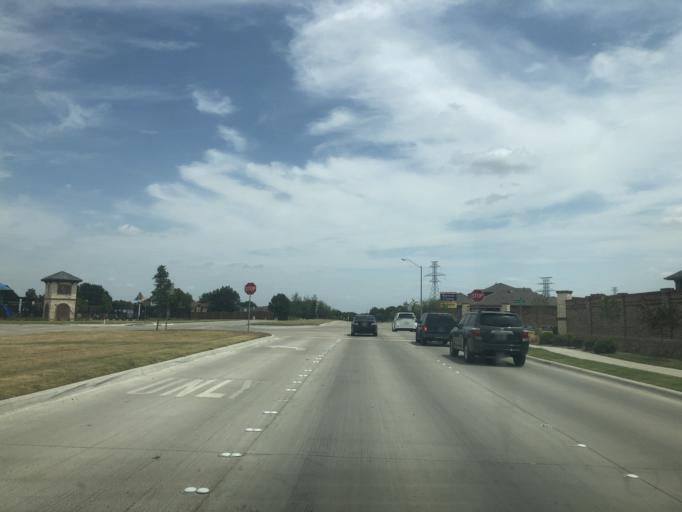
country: US
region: Texas
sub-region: Tarrant County
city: Saginaw
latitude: 32.8783
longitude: -97.3542
